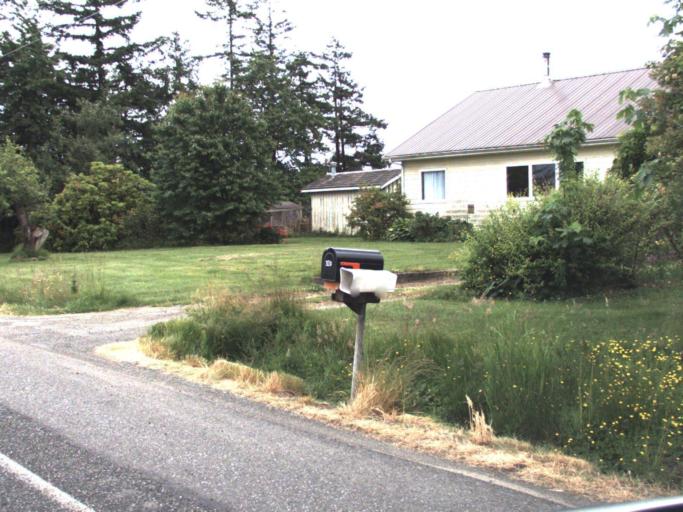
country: US
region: Washington
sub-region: Whatcom County
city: Ferndale
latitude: 48.8918
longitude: -122.6559
